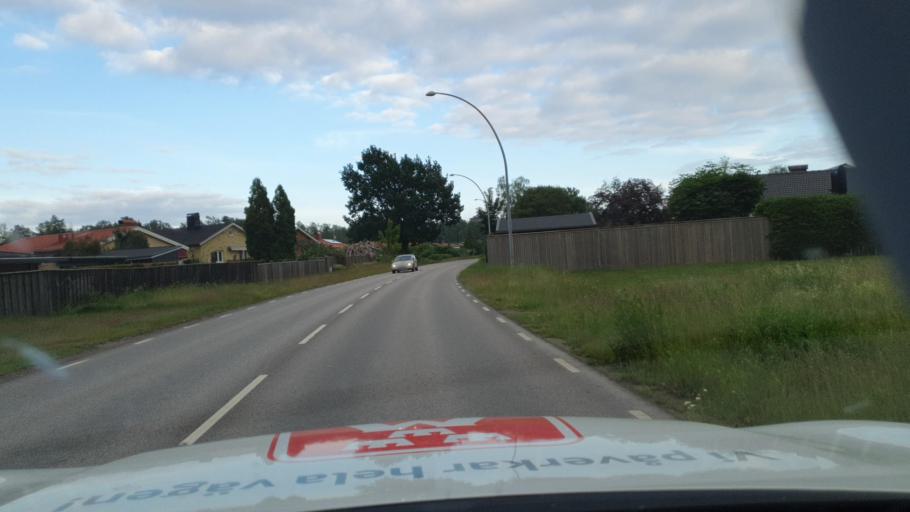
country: SE
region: Vaermland
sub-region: Karlstads Kommun
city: Karlstad
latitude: 59.4044
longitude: 13.5107
